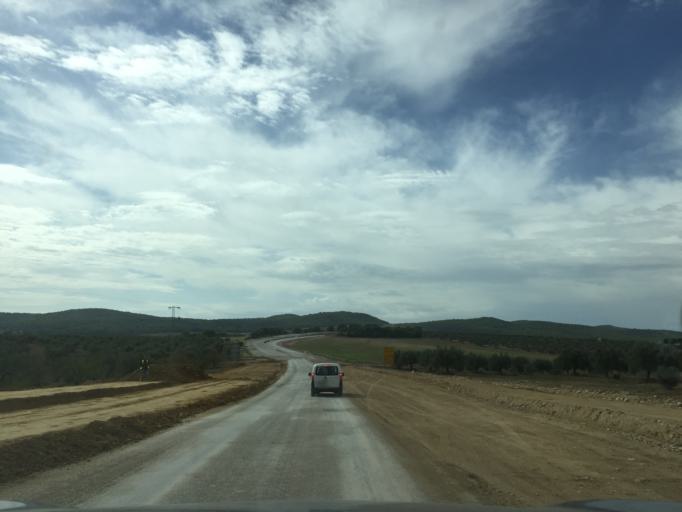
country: TN
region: Zaghwan
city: El Fahs
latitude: 36.2861
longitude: 9.8067
